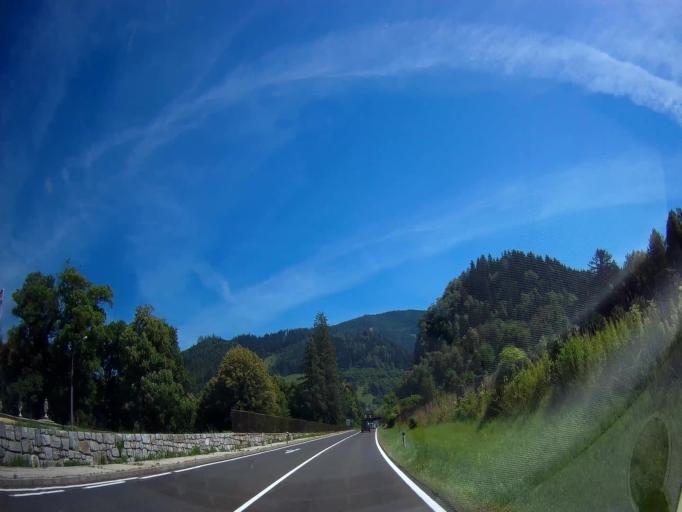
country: AT
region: Carinthia
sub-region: Politischer Bezirk Sankt Veit an der Glan
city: Micheldorf
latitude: 46.8908
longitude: 14.4406
